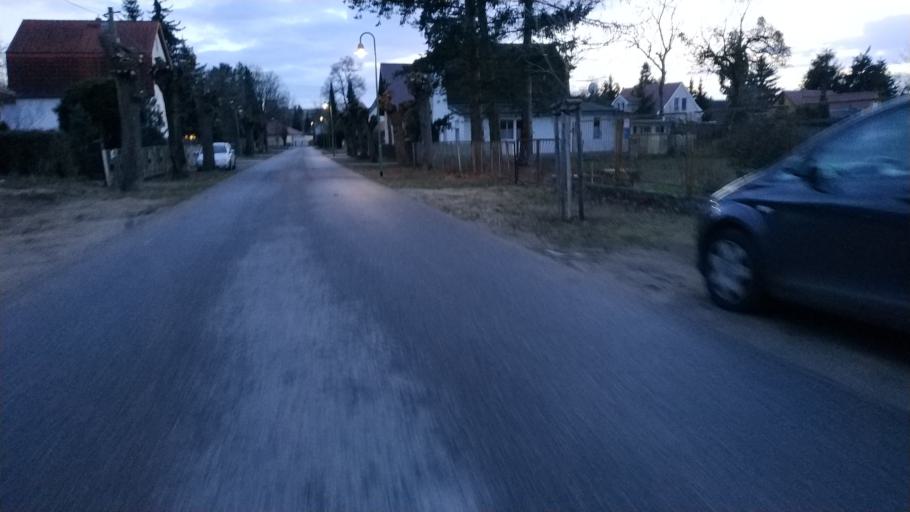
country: DE
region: Brandenburg
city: Petershagen
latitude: 52.5376
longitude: 13.8206
